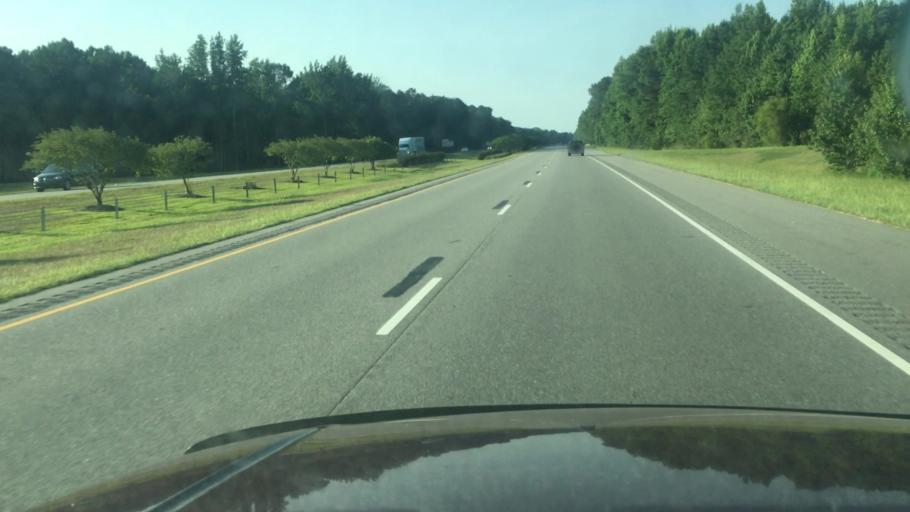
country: US
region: North Carolina
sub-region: Cumberland County
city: Fayetteville
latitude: 35.0080
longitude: -78.8683
